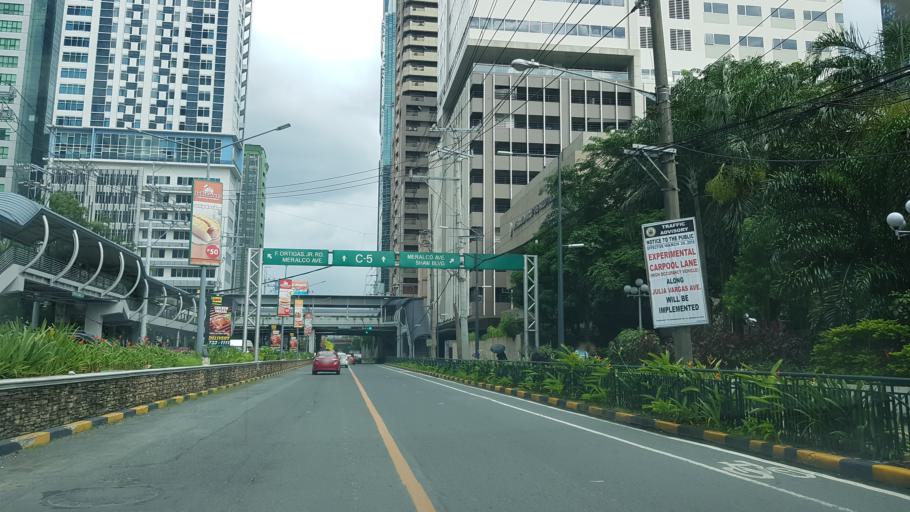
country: PH
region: Metro Manila
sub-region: Pasig
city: Pasig City
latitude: 14.5842
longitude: 121.0604
